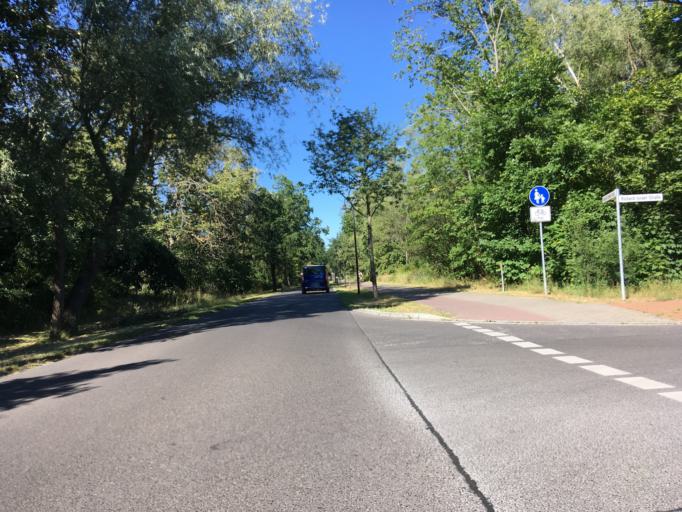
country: DE
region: Brandenburg
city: Schulzendorf
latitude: 52.3647
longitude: 13.5915
